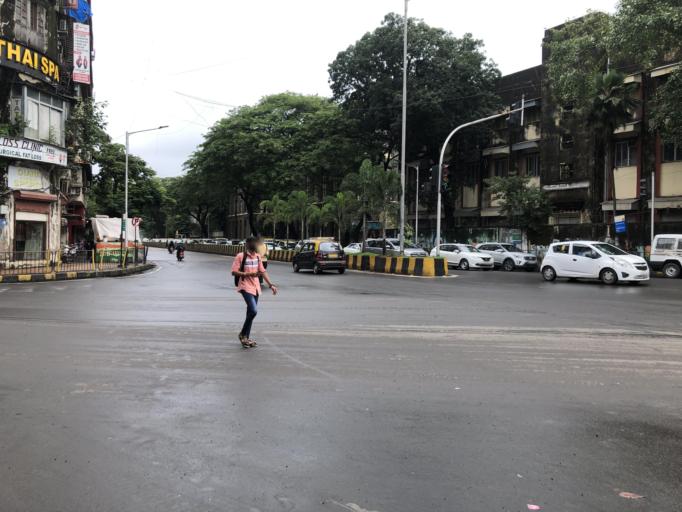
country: IN
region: Maharashtra
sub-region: Raigarh
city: Uran
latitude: 18.9440
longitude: 72.8293
